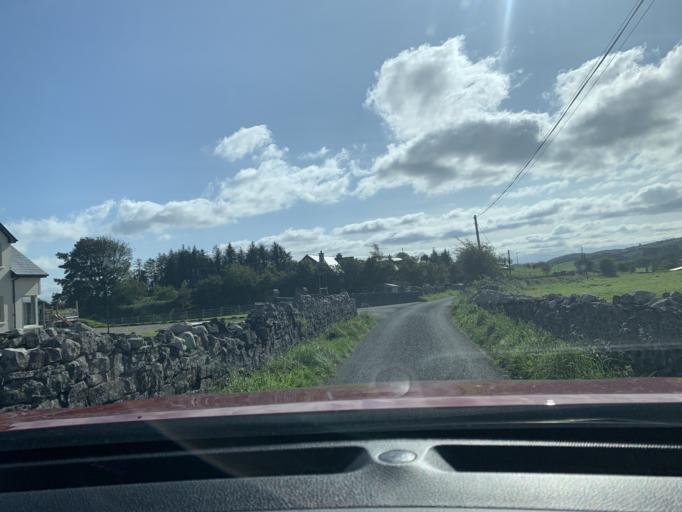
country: IE
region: Connaught
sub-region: Roscommon
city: Boyle
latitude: 54.0817
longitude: -8.3684
